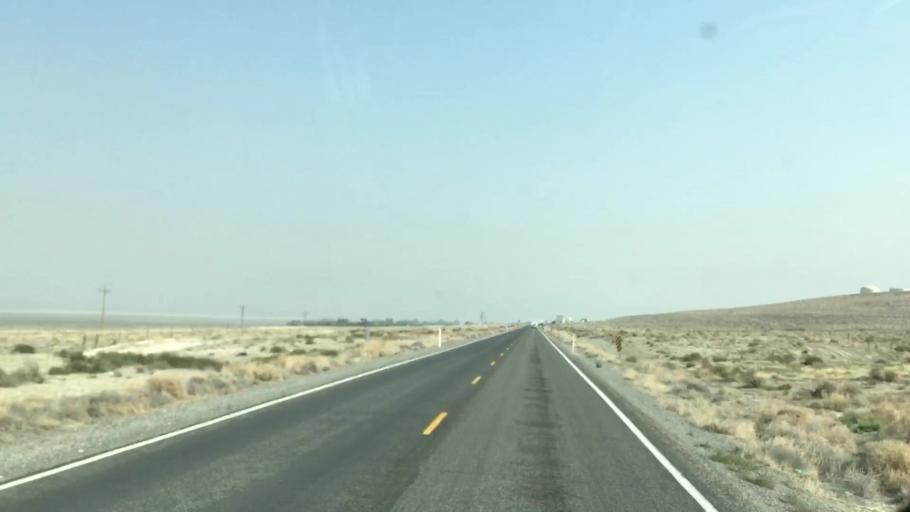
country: US
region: Nevada
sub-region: Pershing County
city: Lovelock
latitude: 40.5602
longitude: -119.3393
